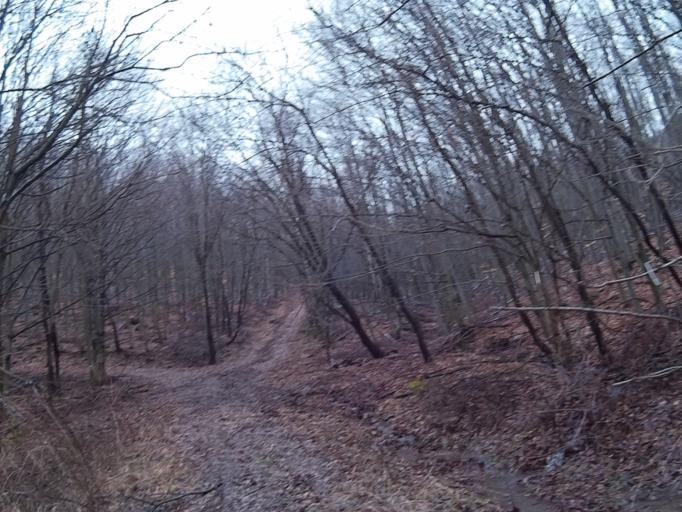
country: HU
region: Borsod-Abauj-Zemplen
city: Gonc
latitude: 48.5546
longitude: 21.4220
